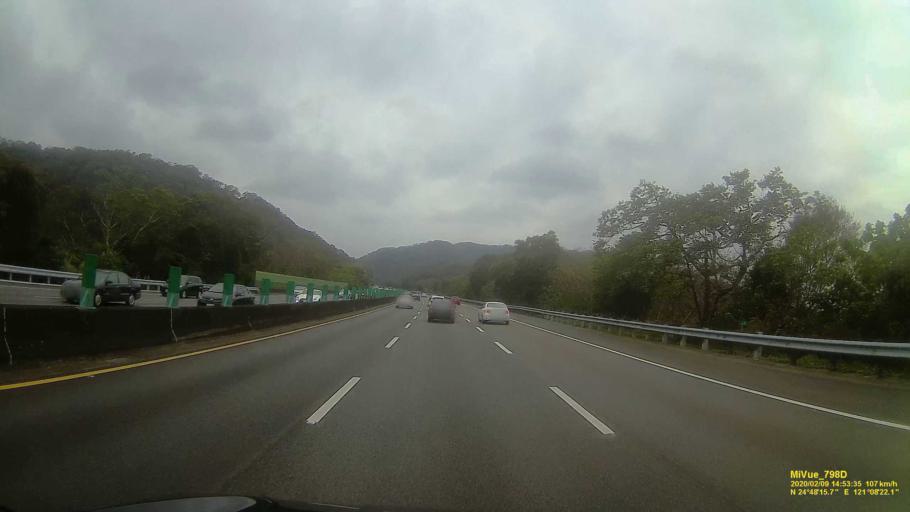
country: TW
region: Taiwan
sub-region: Hsinchu
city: Zhubei
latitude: 24.8041
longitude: 121.1400
